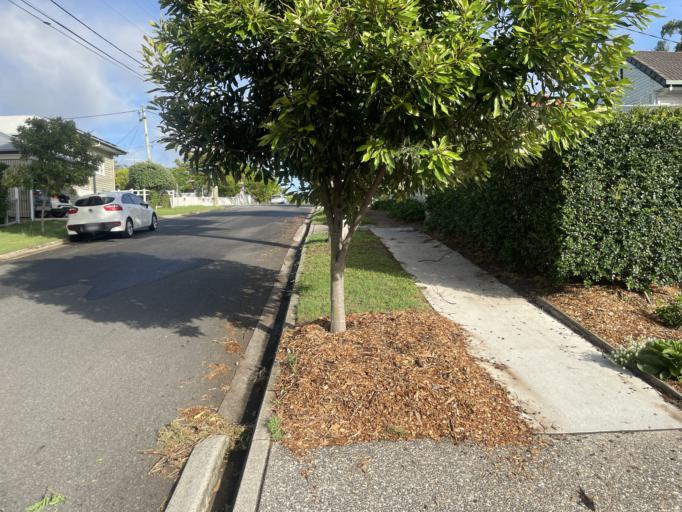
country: AU
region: Queensland
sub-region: Brisbane
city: Greenslopes
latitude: -27.5183
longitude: 153.0714
